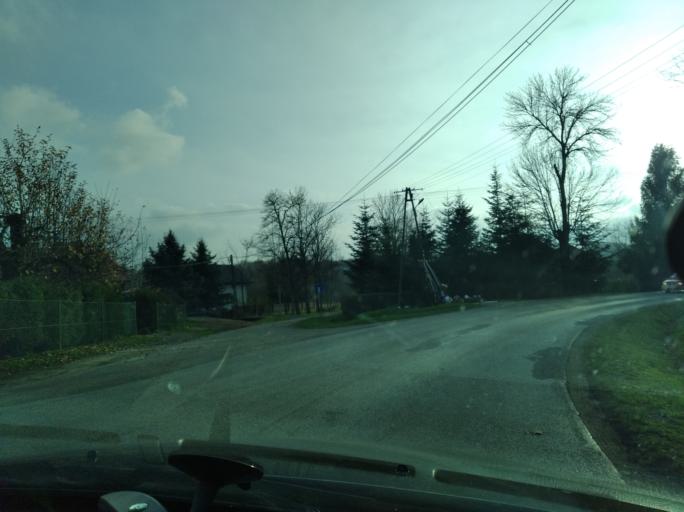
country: PL
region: Subcarpathian Voivodeship
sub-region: Powiat przeworski
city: Lopuszka Wielka
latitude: 49.9425
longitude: 22.4045
